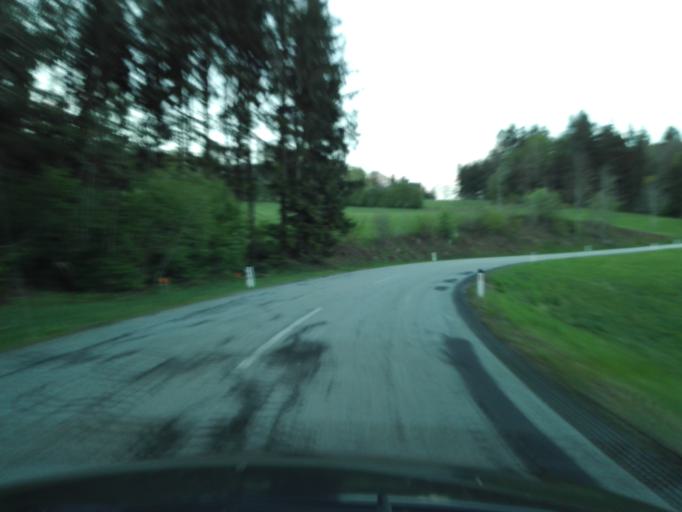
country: DE
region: Bavaria
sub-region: Lower Bavaria
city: Wegscheid
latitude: 48.5537
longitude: 13.7976
